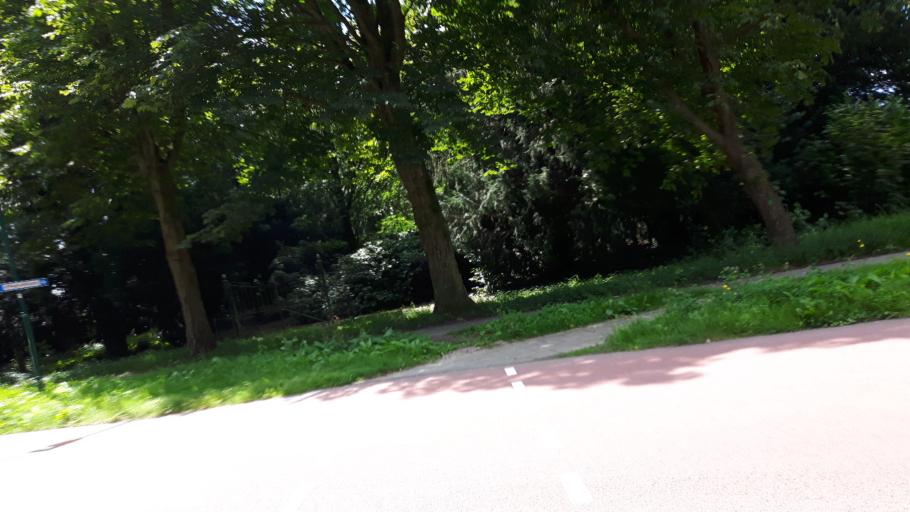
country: NL
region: Utrecht
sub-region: Stichtse Vecht
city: Vreeland
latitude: 52.2126
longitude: 5.0191
